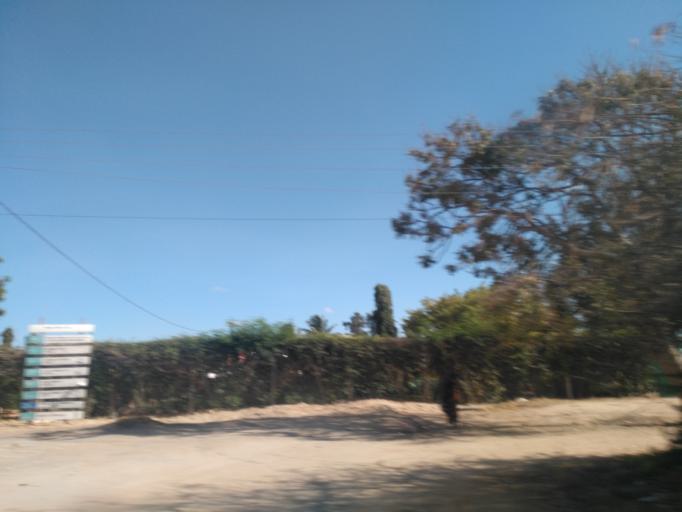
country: TZ
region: Dodoma
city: Dodoma
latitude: -6.1858
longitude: 35.7380
